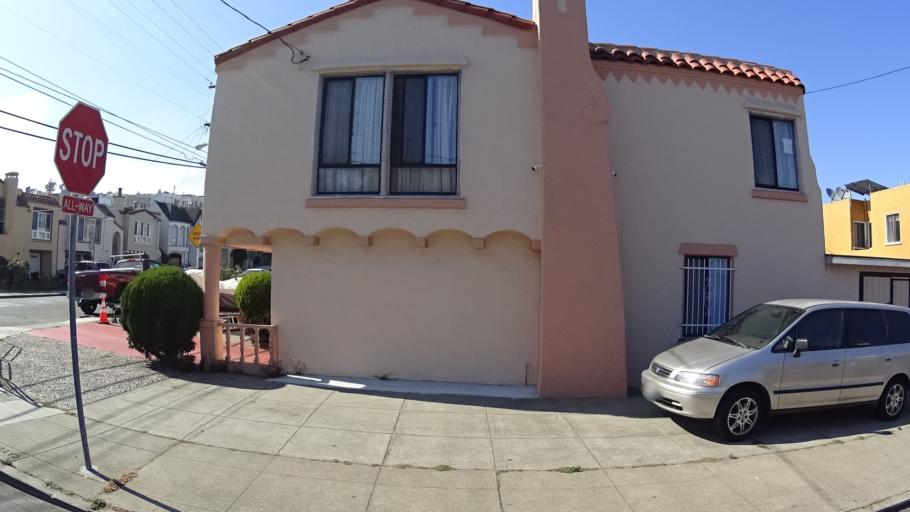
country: US
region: California
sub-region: San Mateo County
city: Daly City
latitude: 37.7181
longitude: -122.4446
